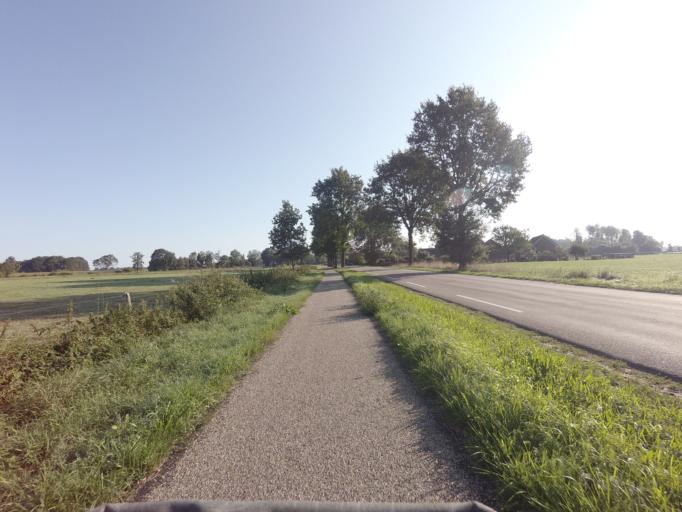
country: NL
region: Overijssel
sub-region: Gemeente Deventer
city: Schalkhaar
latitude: 52.3015
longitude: 6.2678
